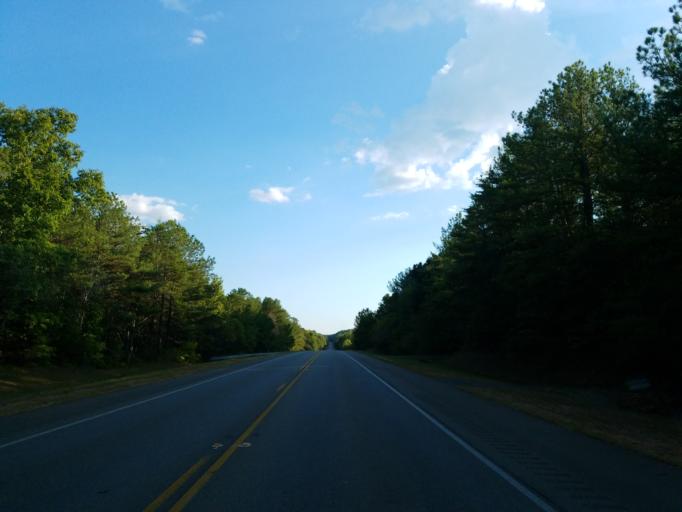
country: US
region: Georgia
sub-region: Murray County
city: Chatsworth
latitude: 34.6302
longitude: -84.7138
